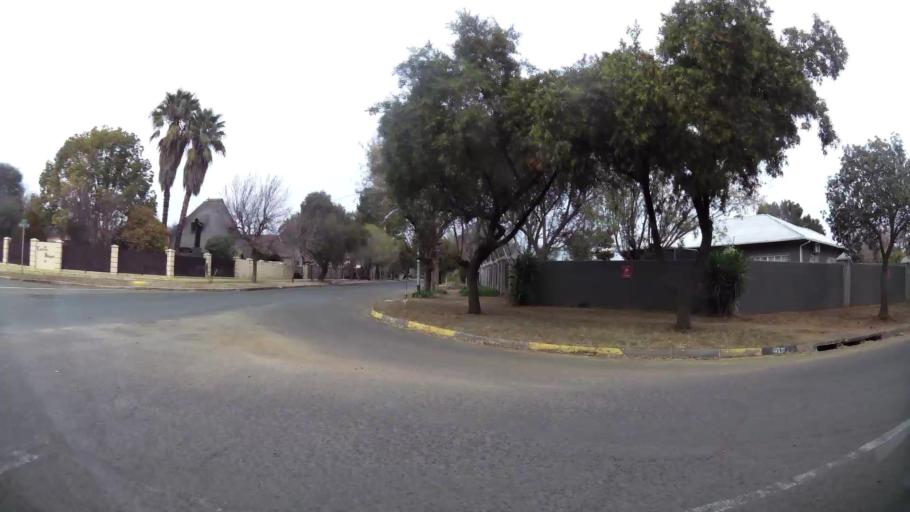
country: ZA
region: Orange Free State
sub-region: Mangaung Metropolitan Municipality
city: Bloemfontein
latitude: -29.1220
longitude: 26.1951
